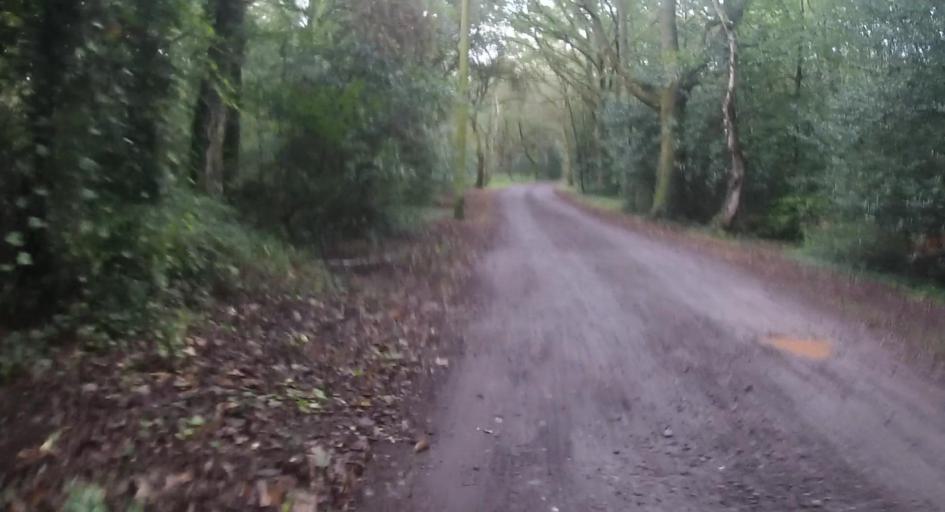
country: GB
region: England
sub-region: West Berkshire
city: Thatcham
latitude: 51.4170
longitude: -1.2289
